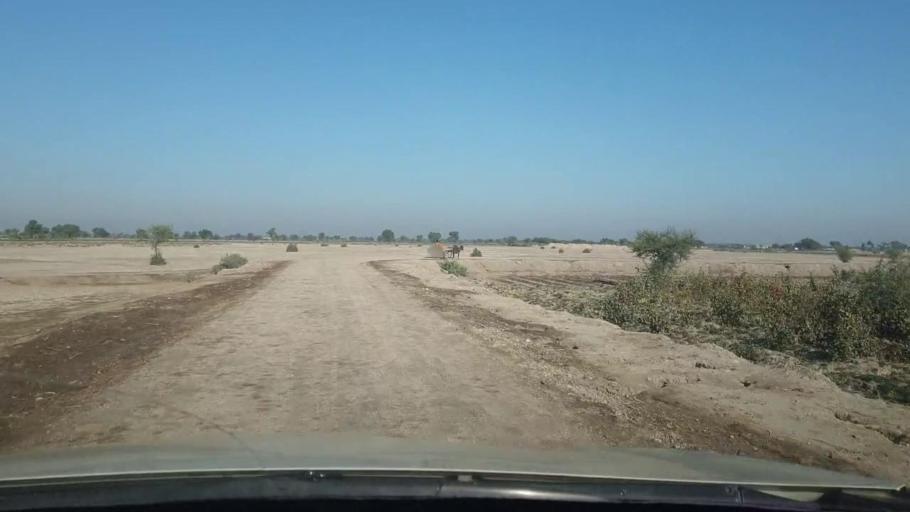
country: PK
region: Sindh
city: Bhan
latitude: 26.5234
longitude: 67.6732
